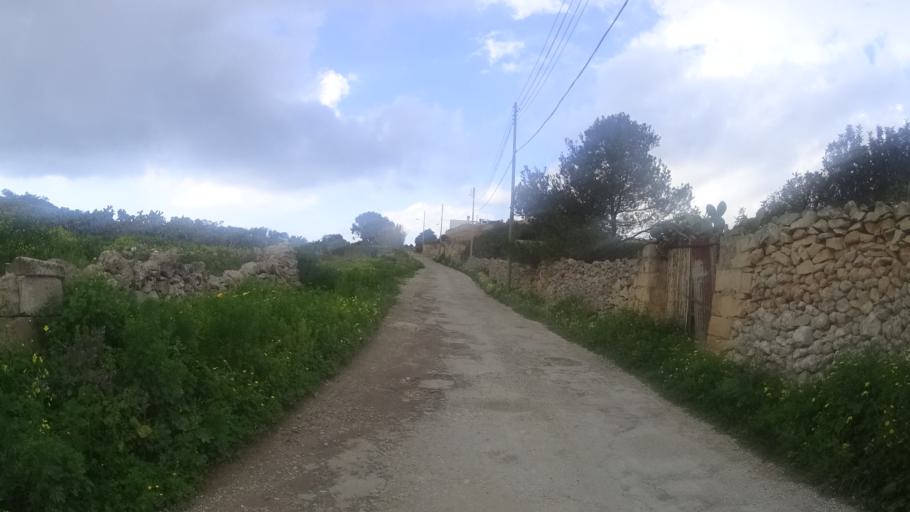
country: MT
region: L-Imgarr
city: Imgarr
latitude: 35.8955
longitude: 14.3687
